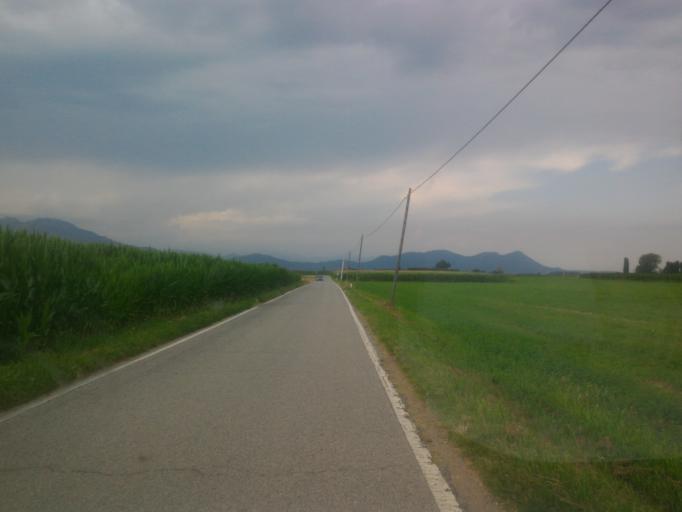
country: IT
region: Piedmont
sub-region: Provincia di Torino
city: Buriasco
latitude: 44.8815
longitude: 7.4021
